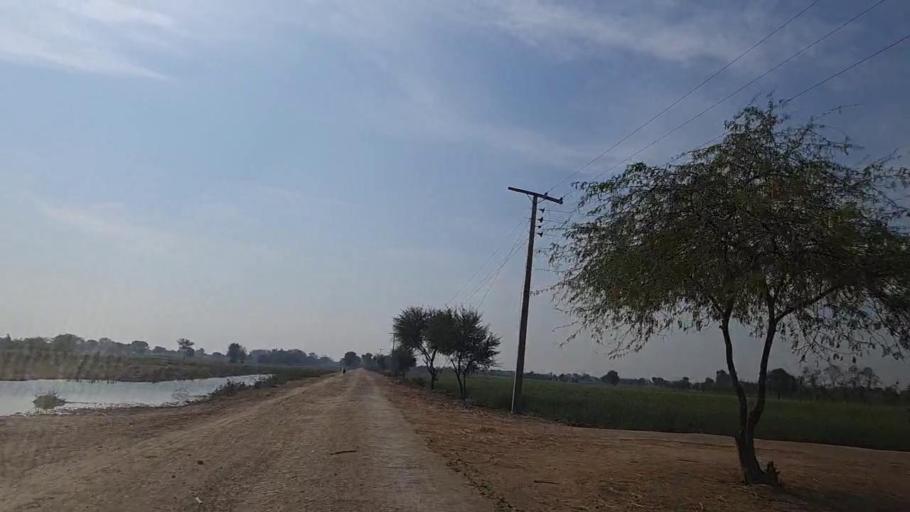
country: PK
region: Sindh
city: Mirpur Khas
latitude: 25.4783
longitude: 68.9745
